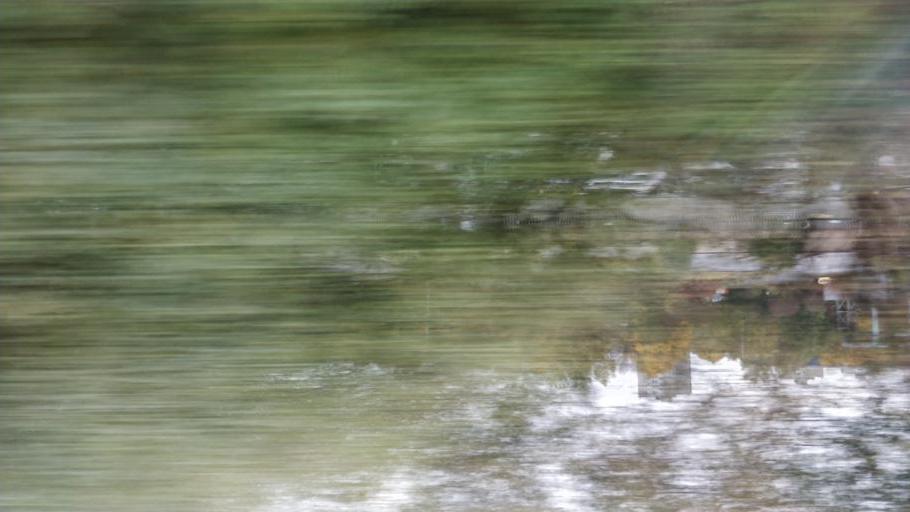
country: GB
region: England
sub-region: Borough of Wigan
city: Ince-in-Makerfield
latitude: 53.5410
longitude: -2.6264
